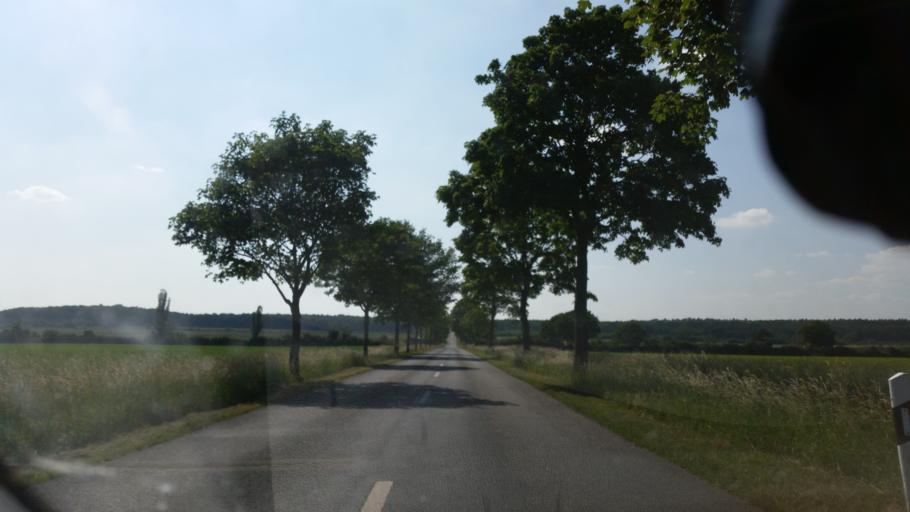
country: DE
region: Lower Saxony
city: Lehre
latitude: 52.3146
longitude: 10.7424
